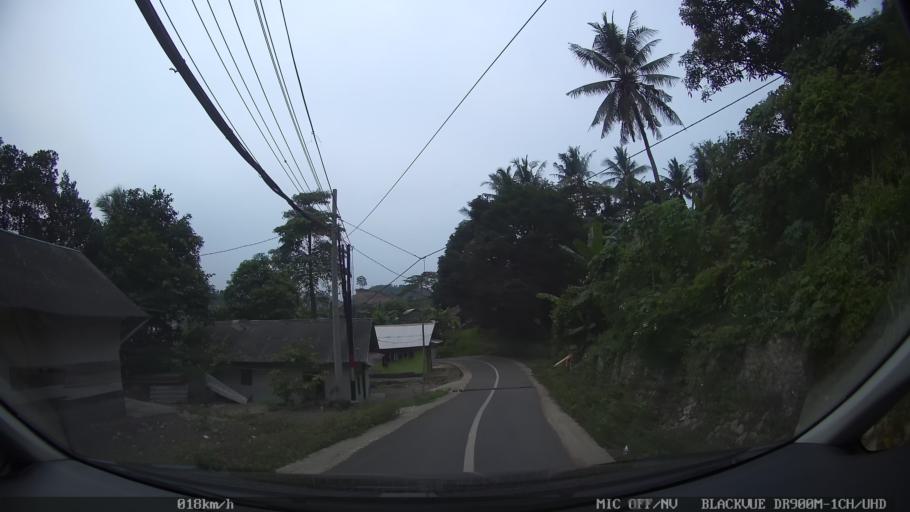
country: ID
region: Lampung
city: Panjang
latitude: -5.4396
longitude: 105.3162
